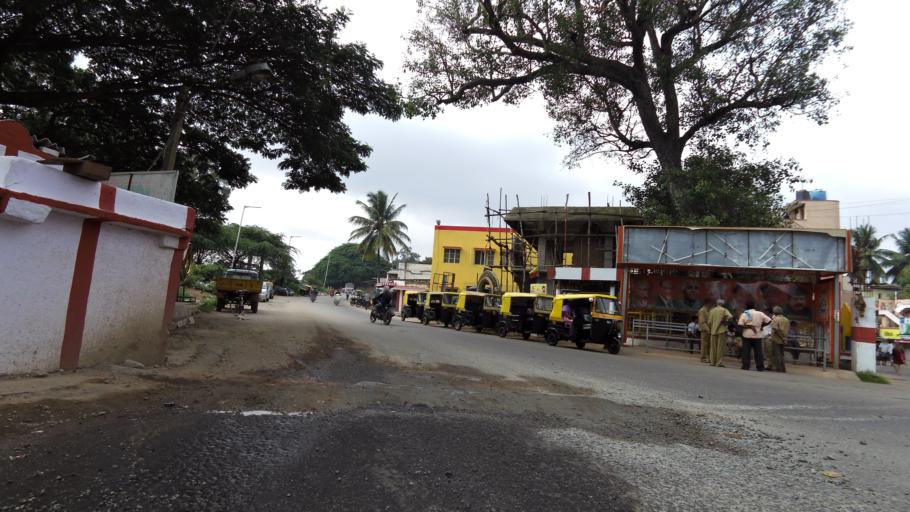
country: IN
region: Karnataka
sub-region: Bangalore Urban
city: Bangalore
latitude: 12.9951
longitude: 77.6436
